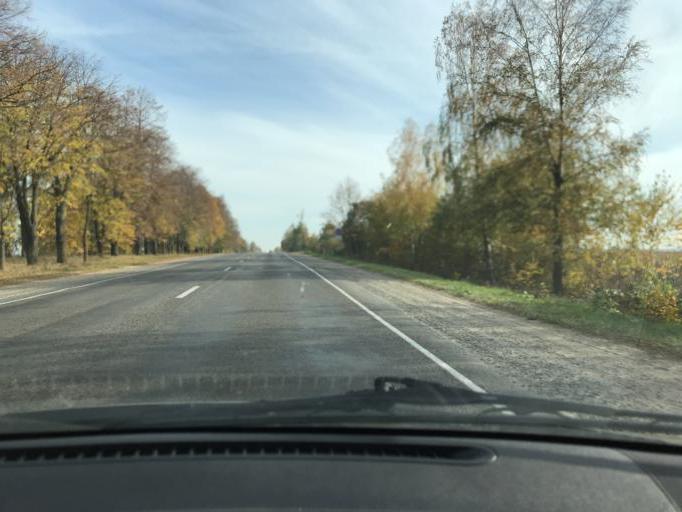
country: BY
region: Brest
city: Asnyezhytsy
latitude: 52.2162
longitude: 26.0395
